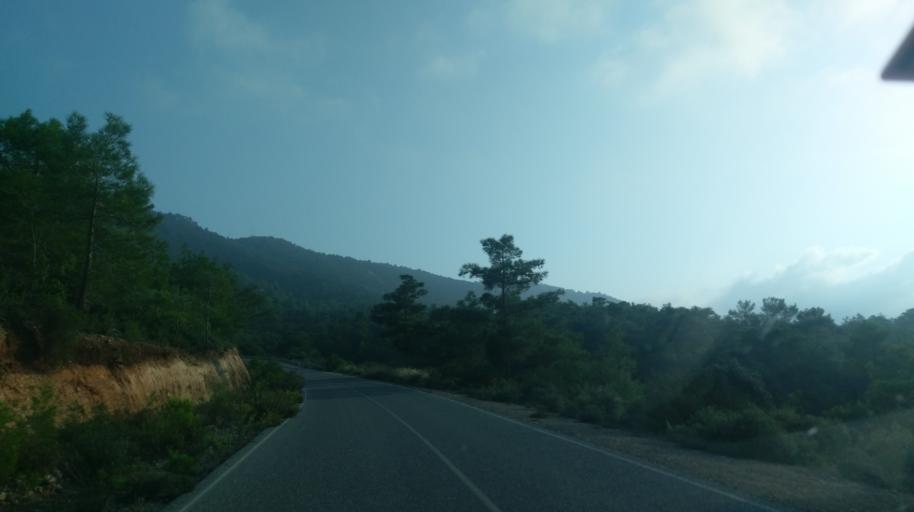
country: CY
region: Ammochostos
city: Trikomo
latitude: 35.4120
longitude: 33.9040
